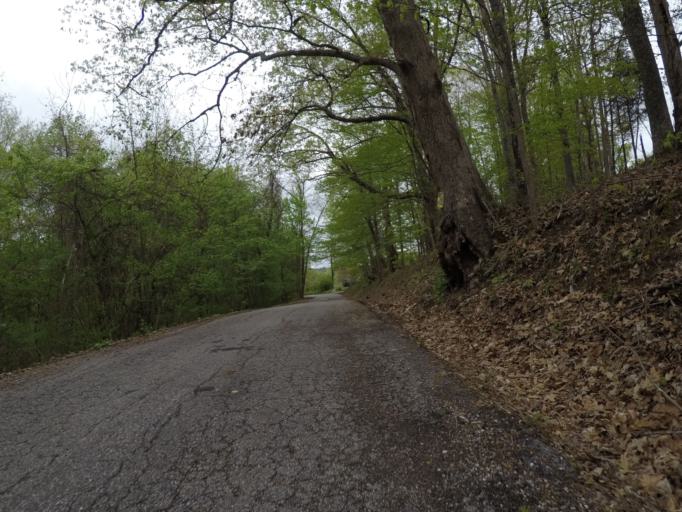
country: US
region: West Virginia
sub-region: Cabell County
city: Barboursville
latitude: 38.3972
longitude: -82.2580
